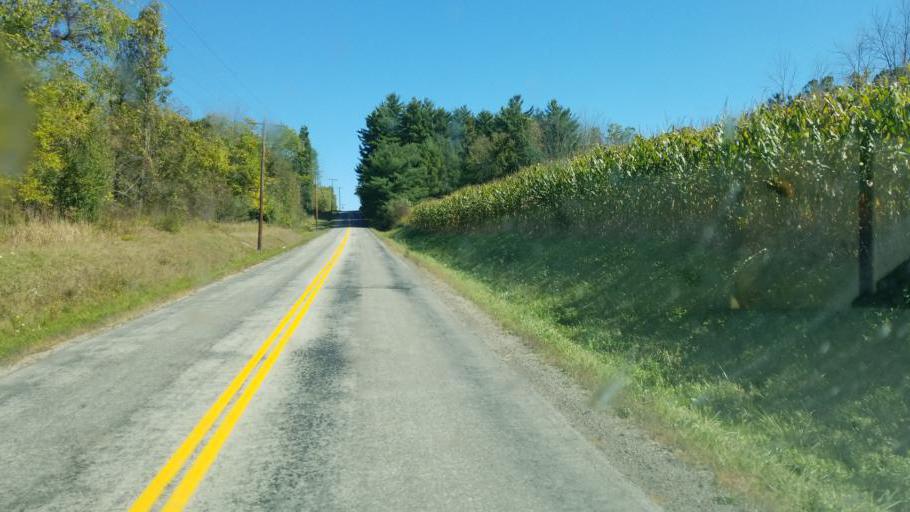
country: US
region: Ohio
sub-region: Huron County
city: New London
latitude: 40.9929
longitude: -82.3941
